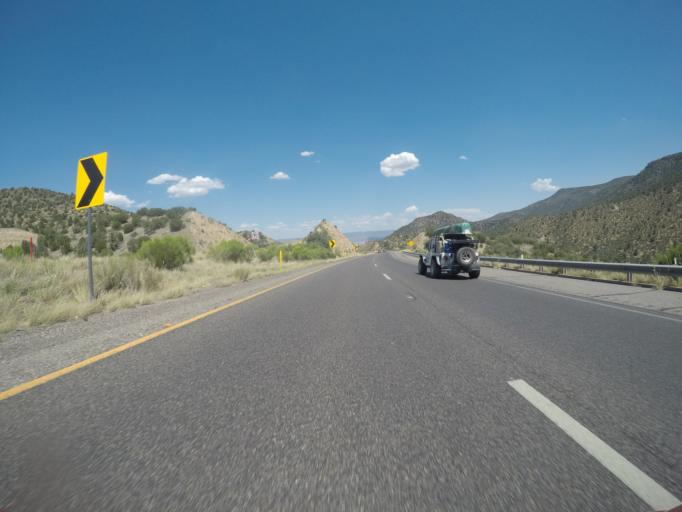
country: US
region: Arizona
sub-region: Yavapai County
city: Camp Verde
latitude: 34.5374
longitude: -111.9229
